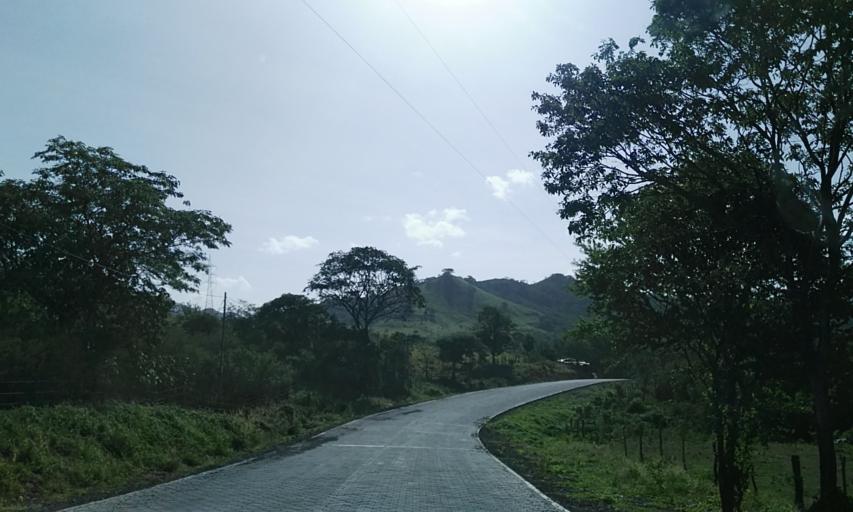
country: NI
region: Matagalpa
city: Ciudad Dario
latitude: 12.7324
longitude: -86.0592
